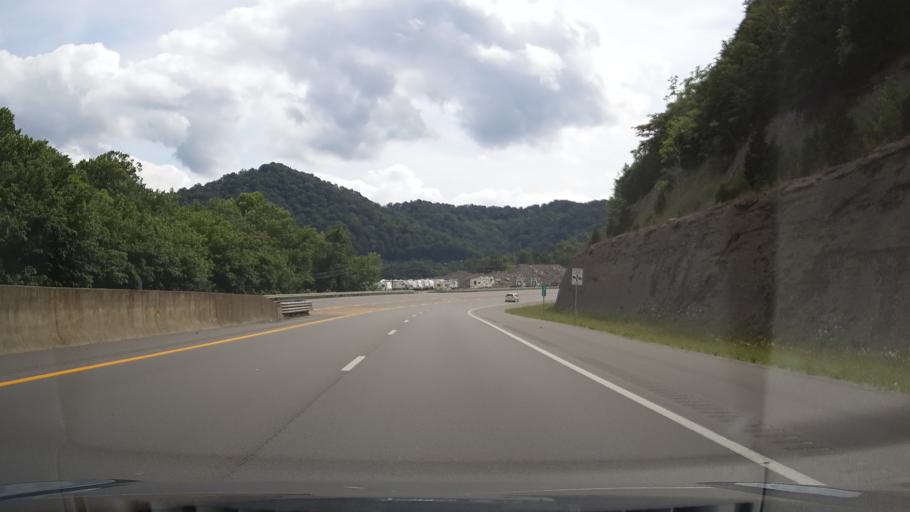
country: US
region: Kentucky
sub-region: Pike County
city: Coal Run Village
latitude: 37.5382
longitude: -82.5947
